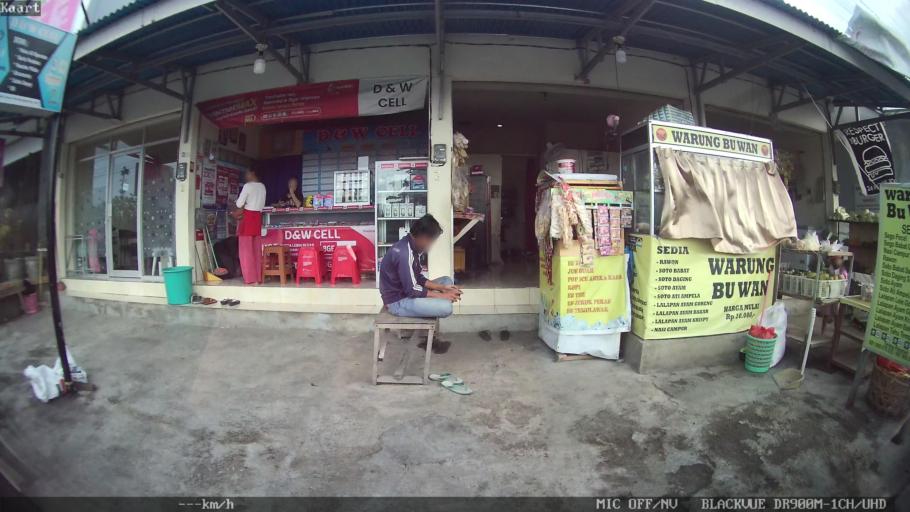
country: ID
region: Bali
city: Karyadharma
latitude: -8.6996
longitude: 115.1943
